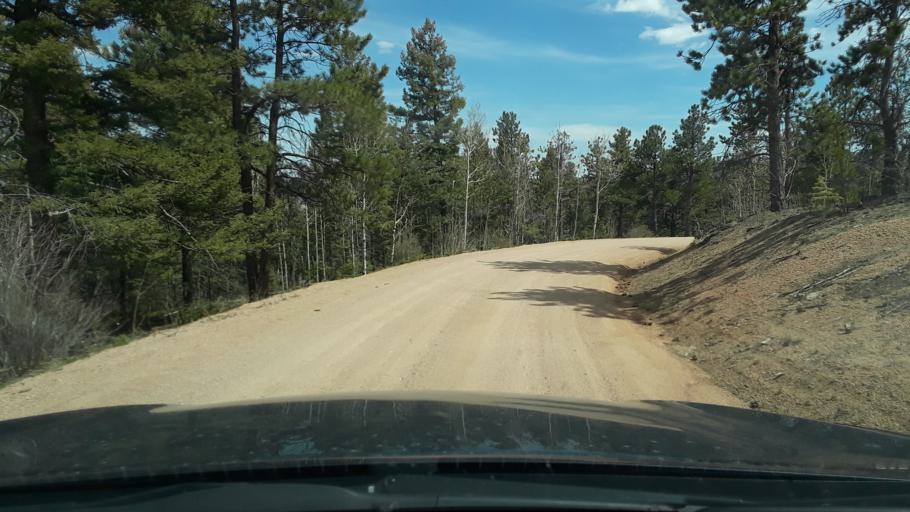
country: US
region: Colorado
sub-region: El Paso County
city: Palmer Lake
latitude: 39.0700
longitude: -104.9498
